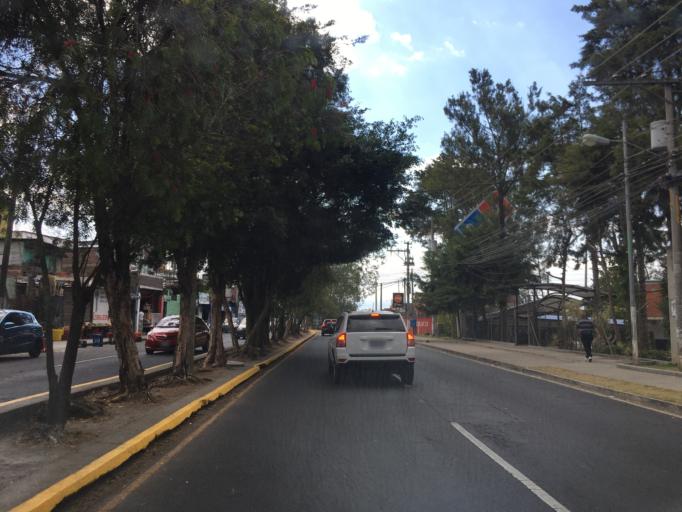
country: GT
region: Guatemala
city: Guatemala City
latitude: 14.6250
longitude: -90.4731
